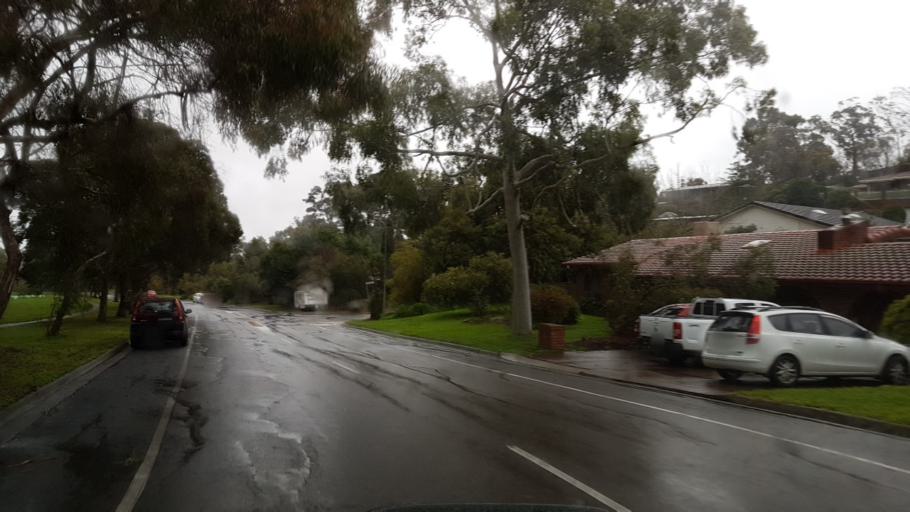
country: AU
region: South Australia
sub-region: Onkaparinga
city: Craigburn Farm
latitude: -35.0908
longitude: 138.5925
